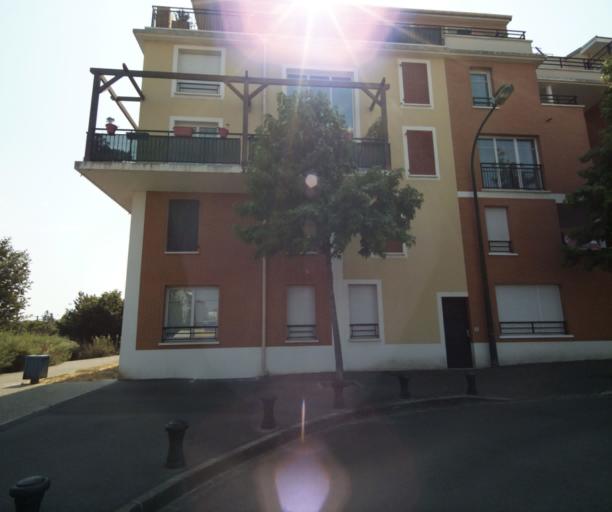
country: FR
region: Ile-de-France
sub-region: Departement des Yvelines
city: Conflans-Sainte-Honorine
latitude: 48.9992
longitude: 2.1035
